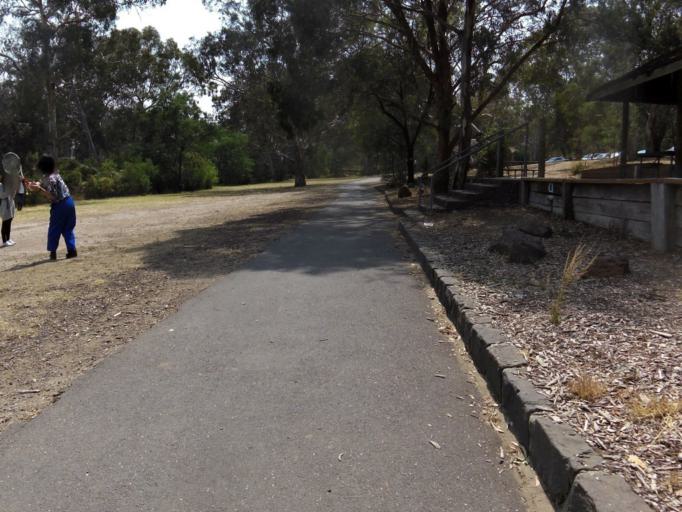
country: AU
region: Victoria
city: Abbotsford
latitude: -37.8009
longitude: 145.0086
